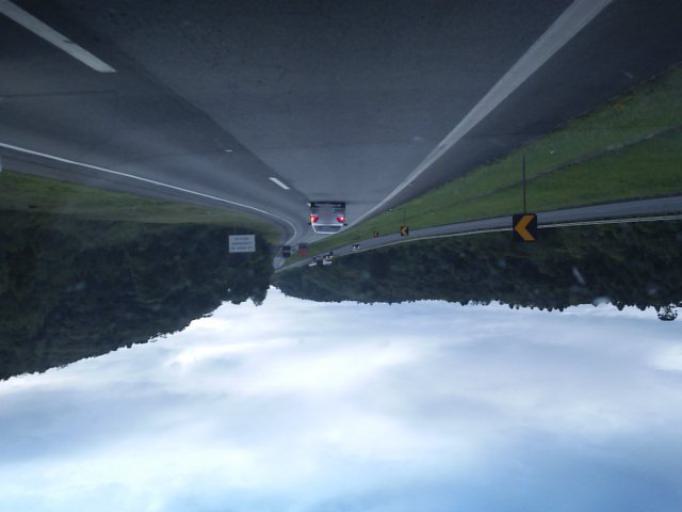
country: BR
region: Parana
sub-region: Campina Grande Do Sul
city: Campina Grande do Sul
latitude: -25.2631
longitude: -48.9149
